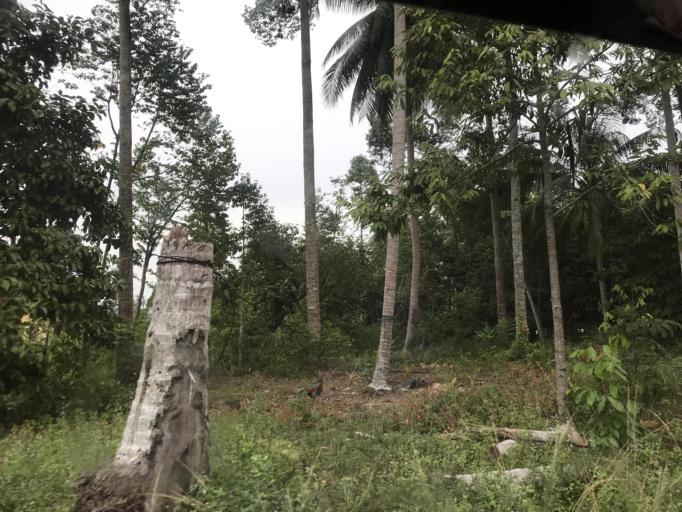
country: MY
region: Kelantan
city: Tumpat
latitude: 6.1681
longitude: 102.2014
